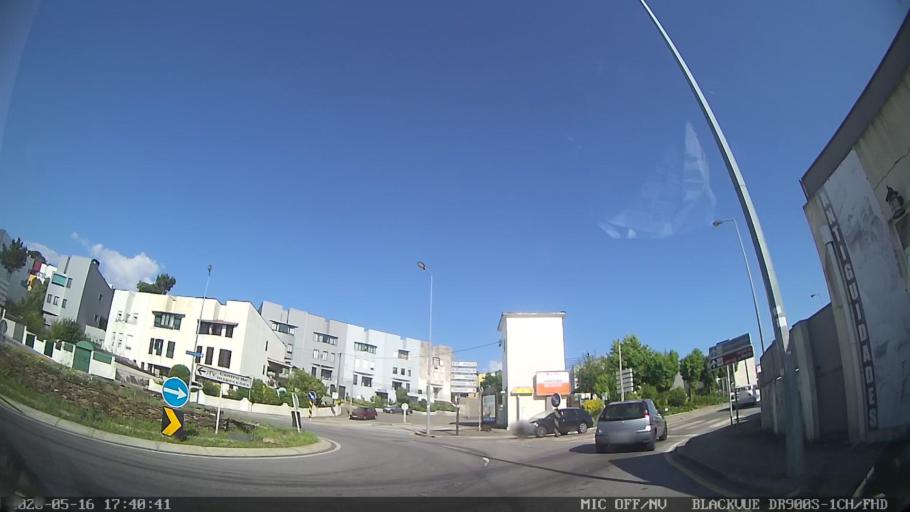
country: PT
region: Porto
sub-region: Valongo
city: Valongo
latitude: 41.1910
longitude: -8.5187
